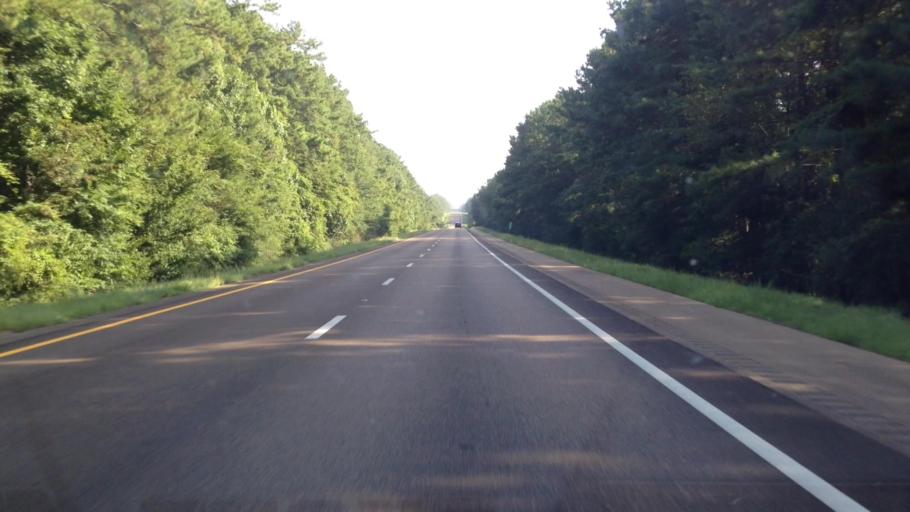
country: US
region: Mississippi
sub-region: Pike County
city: Summit
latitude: 31.3747
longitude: -90.4791
